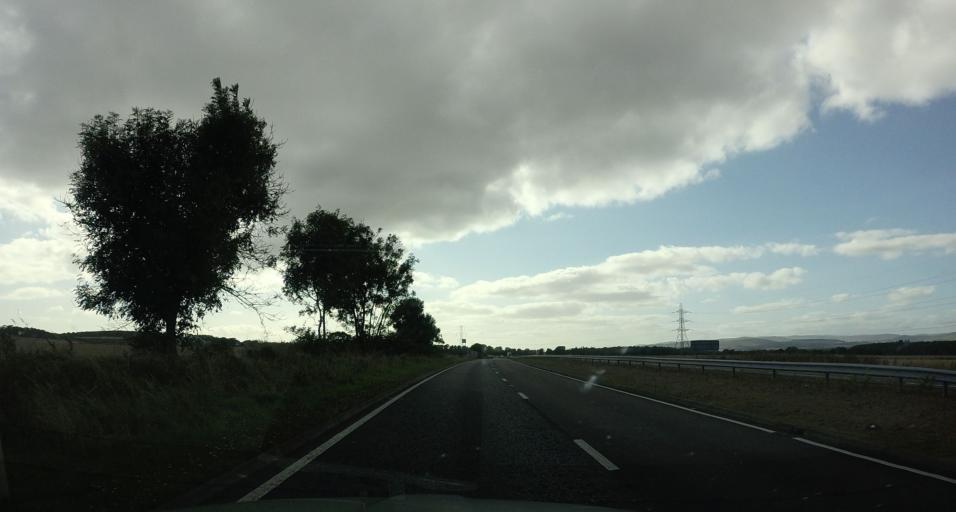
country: GB
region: Scotland
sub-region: Angus
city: Brechin
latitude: 56.7834
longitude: -2.5794
